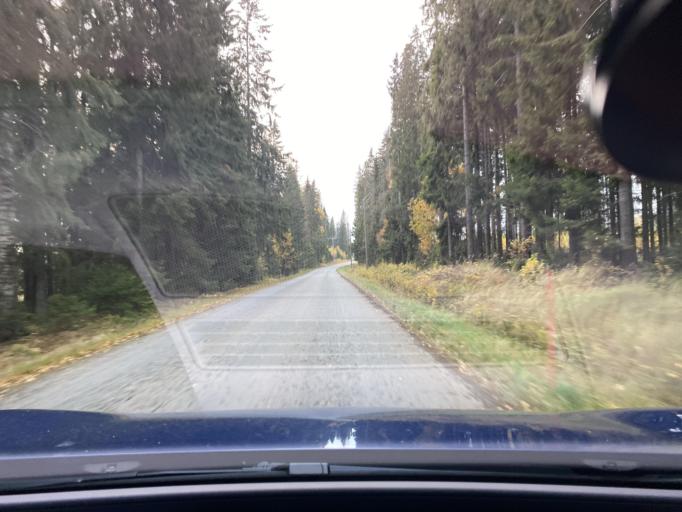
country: FI
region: Varsinais-Suomi
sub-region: Loimaa
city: Alastaro
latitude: 61.0811
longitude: 22.9463
